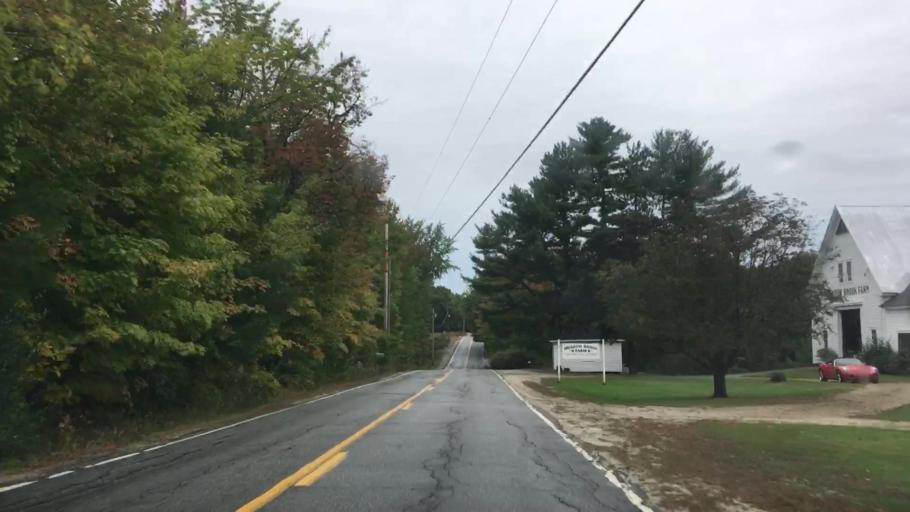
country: US
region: Maine
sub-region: Cumberland County
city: Raymond
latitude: 43.9715
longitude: -70.4684
